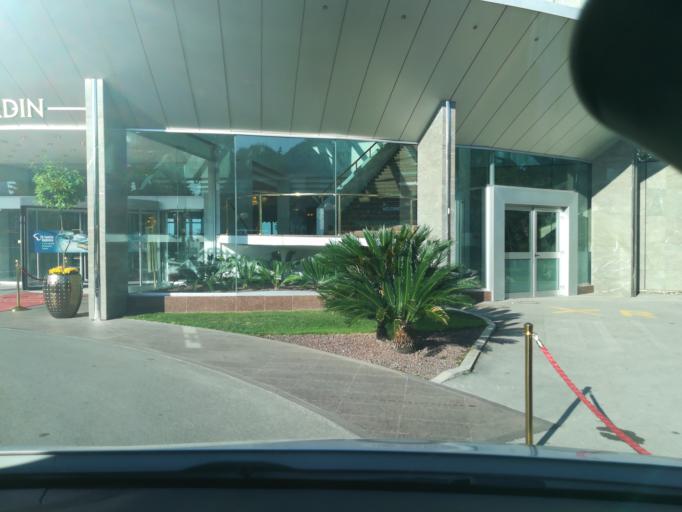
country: SI
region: Piran-Pirano
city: Piran
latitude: 45.5172
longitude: 13.5699
